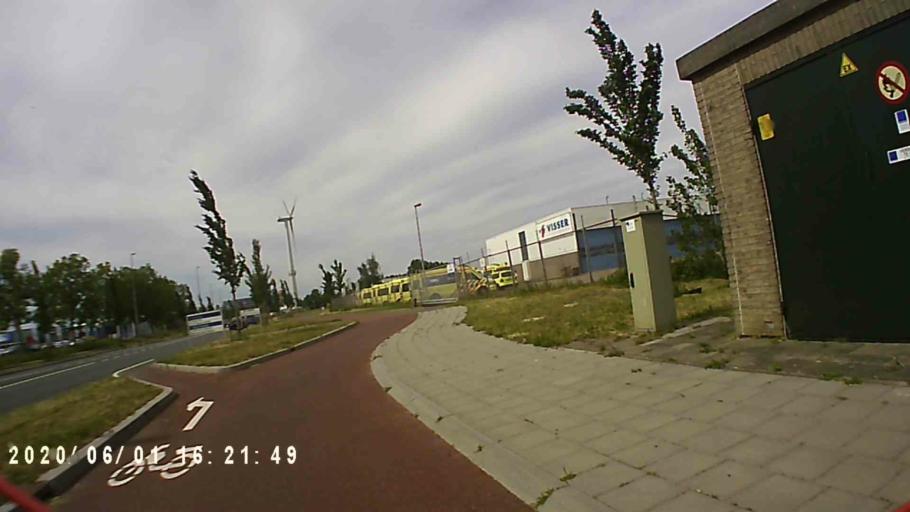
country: NL
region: Friesland
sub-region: Gemeente Leeuwarden
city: Camminghaburen
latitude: 53.1959
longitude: 5.8483
